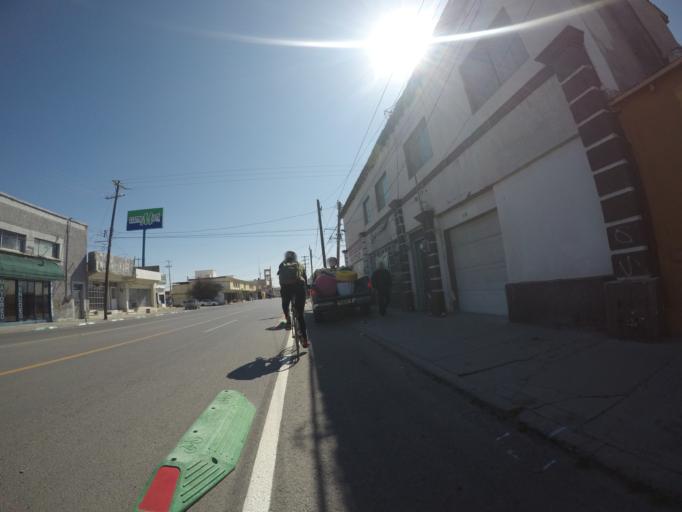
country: MX
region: Chihuahua
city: Ciudad Juarez
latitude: 31.7330
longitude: -106.4691
